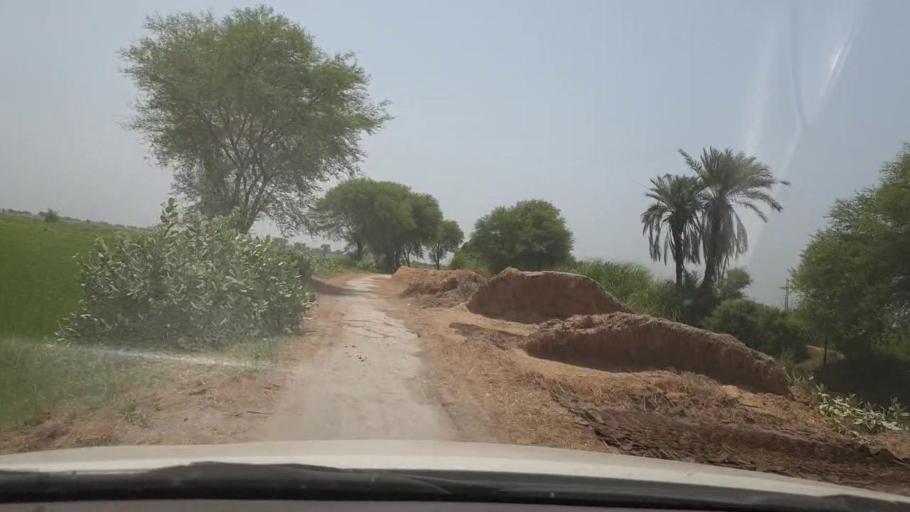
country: PK
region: Sindh
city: Shikarpur
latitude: 28.0780
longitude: 68.5495
